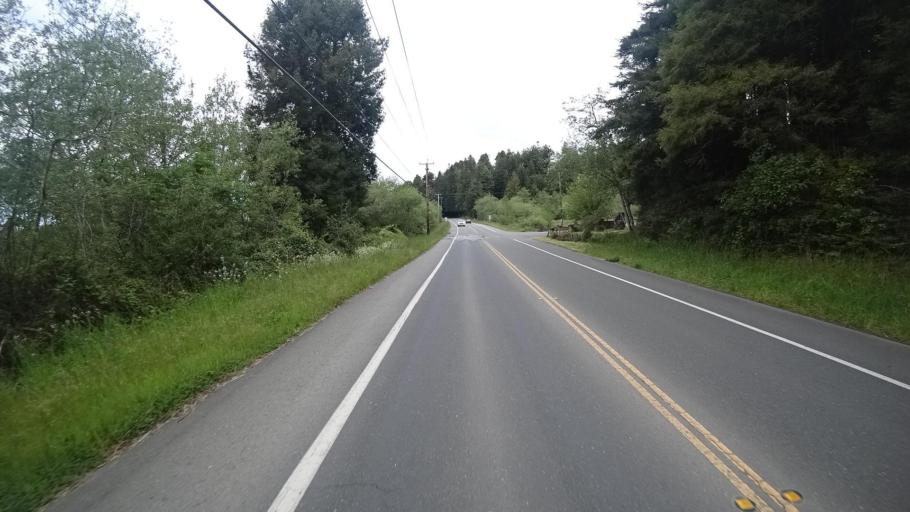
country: US
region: California
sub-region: Humboldt County
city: Bayside
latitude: 40.8258
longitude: -124.0769
